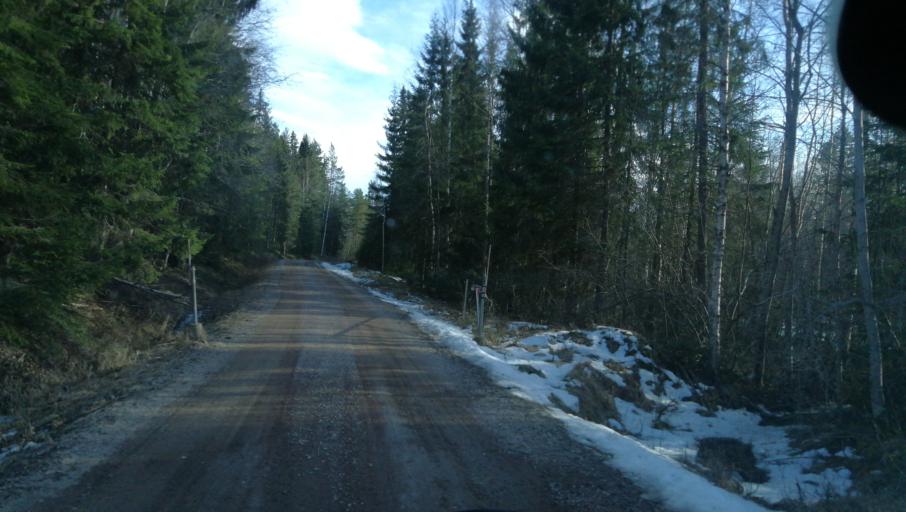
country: SE
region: Dalarna
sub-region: Vansbro Kommun
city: Vansbro
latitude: 60.8218
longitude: 14.1947
